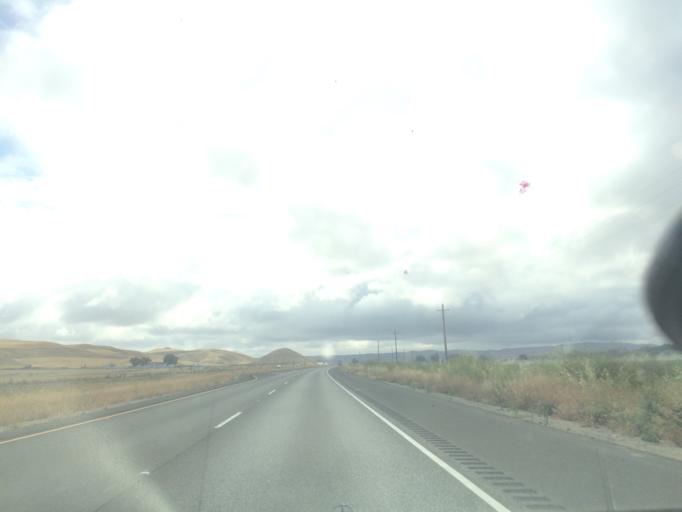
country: US
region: California
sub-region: San Luis Obispo County
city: Shandon
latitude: 35.6613
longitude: -120.4364
